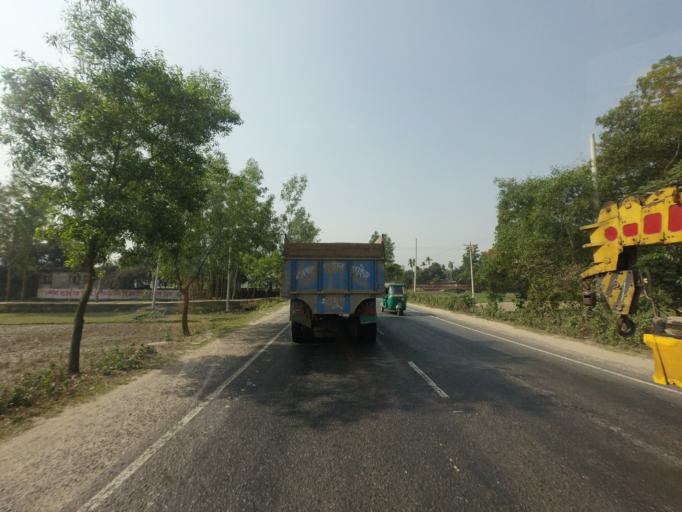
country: BD
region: Sylhet
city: Habiganj
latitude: 24.3935
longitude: 91.5593
